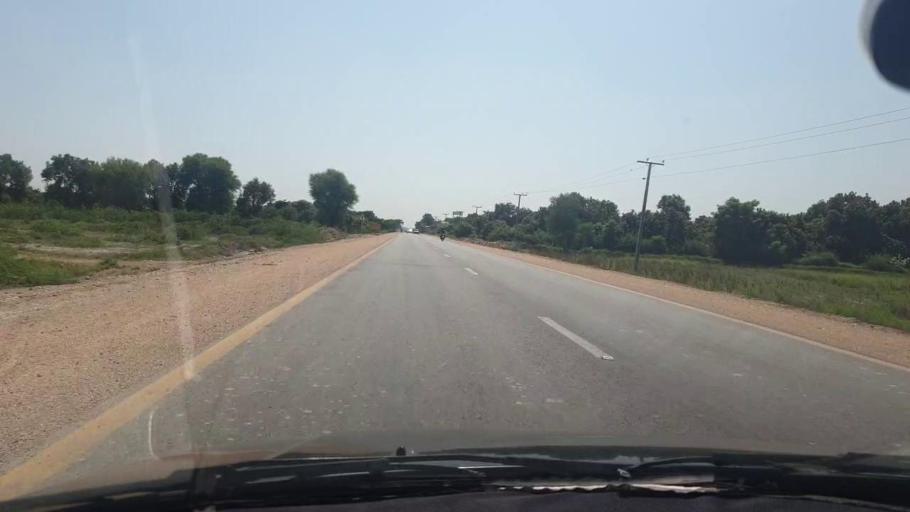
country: PK
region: Sindh
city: Chambar
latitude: 25.3243
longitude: 68.8009
